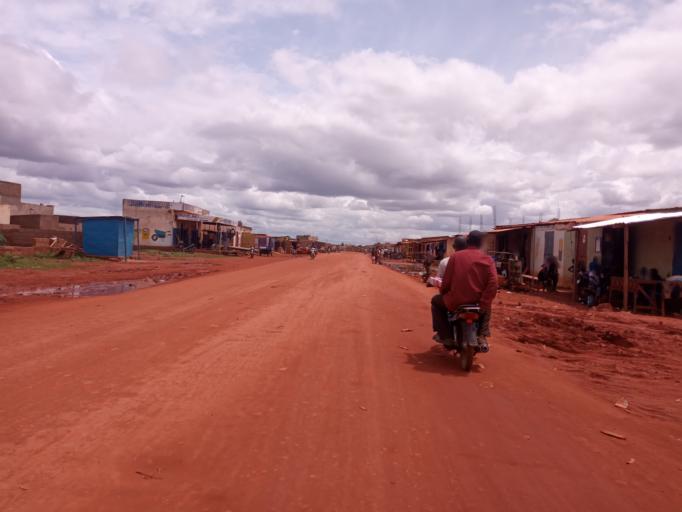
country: ML
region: Bamako
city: Bamako
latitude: 12.5345
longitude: -7.9943
